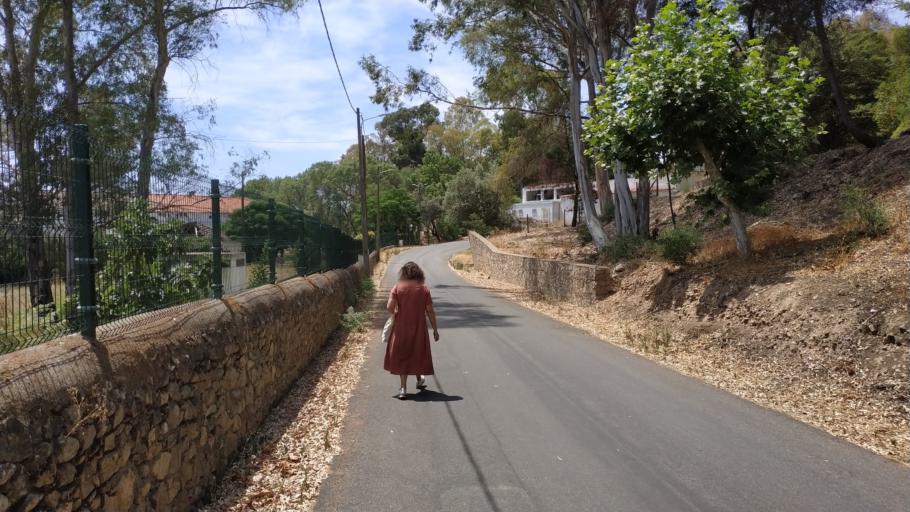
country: ES
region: Extremadura
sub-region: Provincia de Caceres
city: Zarza la Mayor
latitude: 39.9996
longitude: -6.8757
